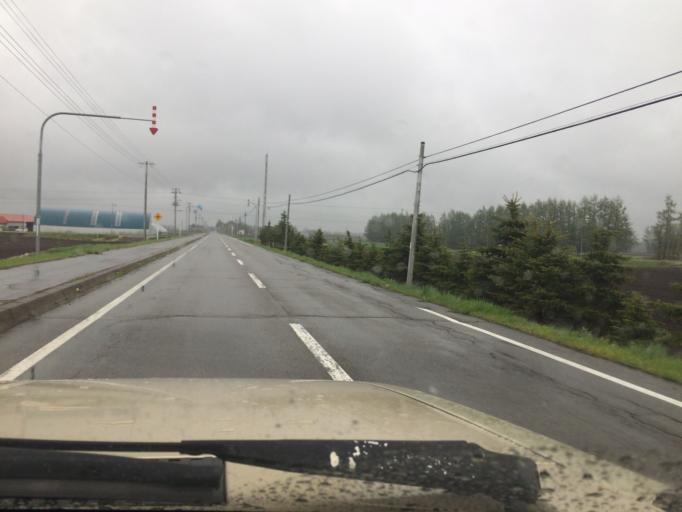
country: JP
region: Hokkaido
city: Obihiro
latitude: 42.8554
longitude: 143.0077
